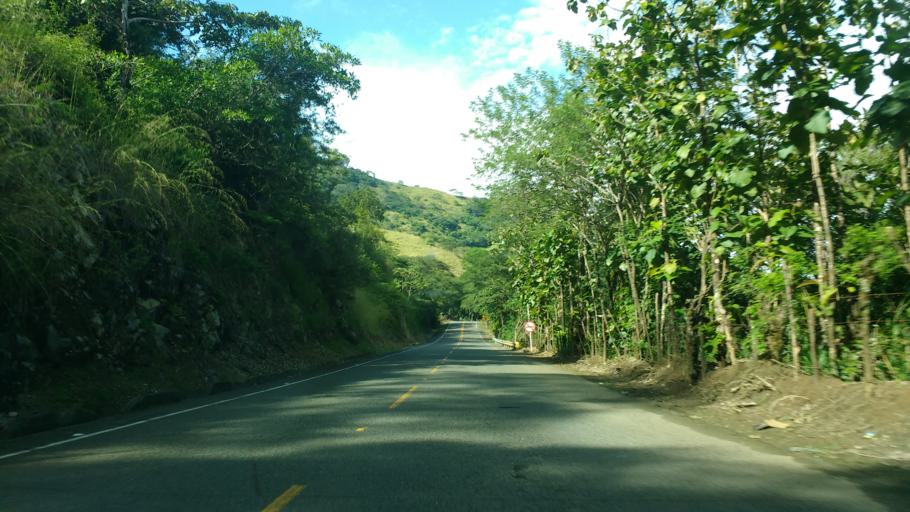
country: CO
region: Antioquia
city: Concordia
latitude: 6.0547
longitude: -75.8667
